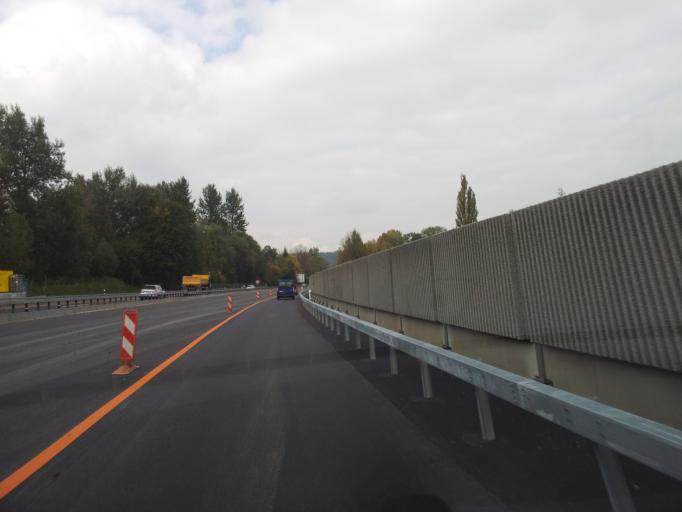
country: CH
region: Bern
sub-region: Bern-Mittelland District
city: Rubigen
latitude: 46.8944
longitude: 7.5353
